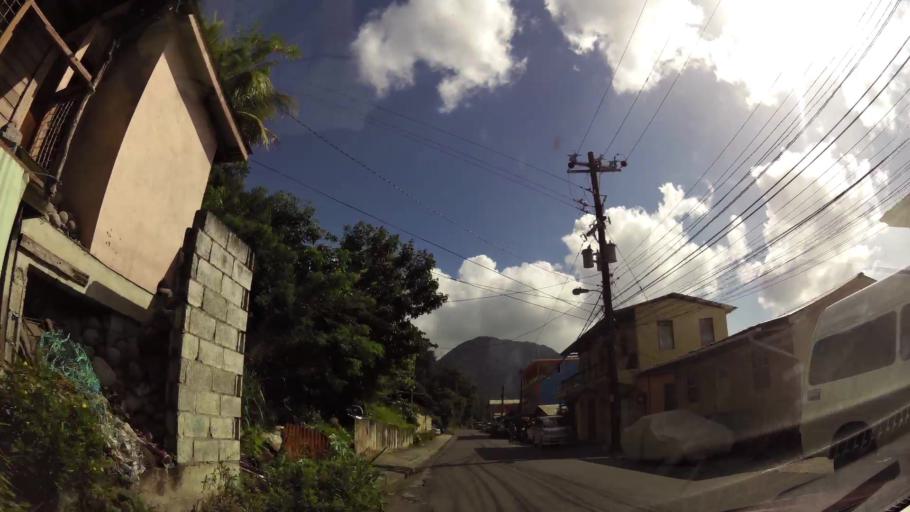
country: DM
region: Saint George
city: Roseau
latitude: 15.2890
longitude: -61.3767
